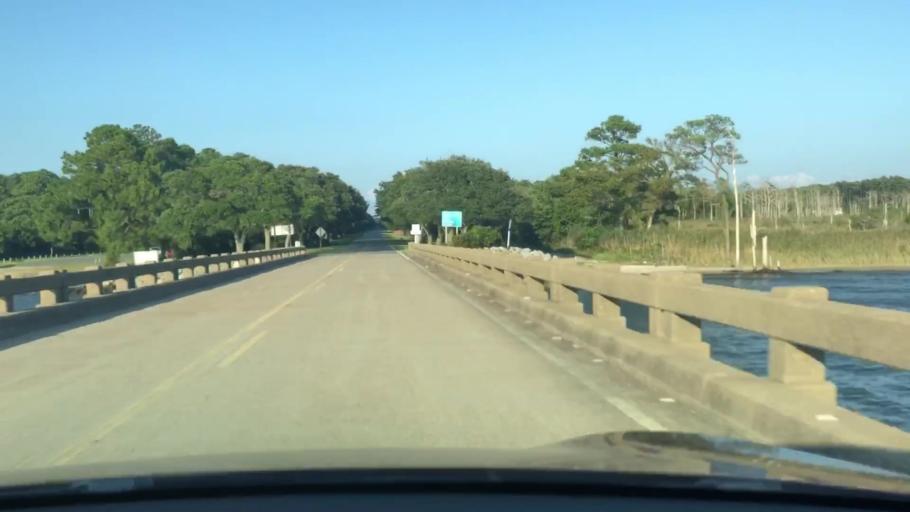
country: US
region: North Carolina
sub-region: Dare County
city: Manteo
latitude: 35.9270
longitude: -75.7242
